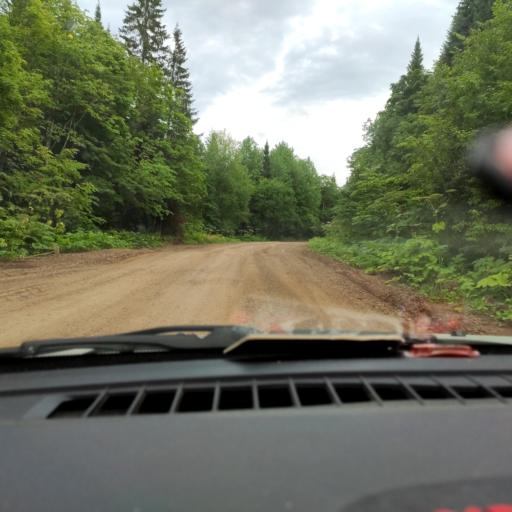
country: RU
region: Perm
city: Kultayevo
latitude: 57.8119
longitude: 56.0038
